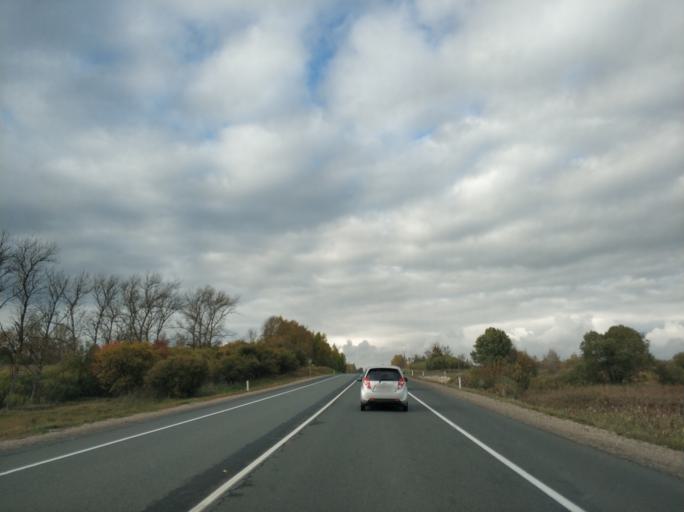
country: RU
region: Pskov
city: Ostrov
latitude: 57.4177
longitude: 28.3626
